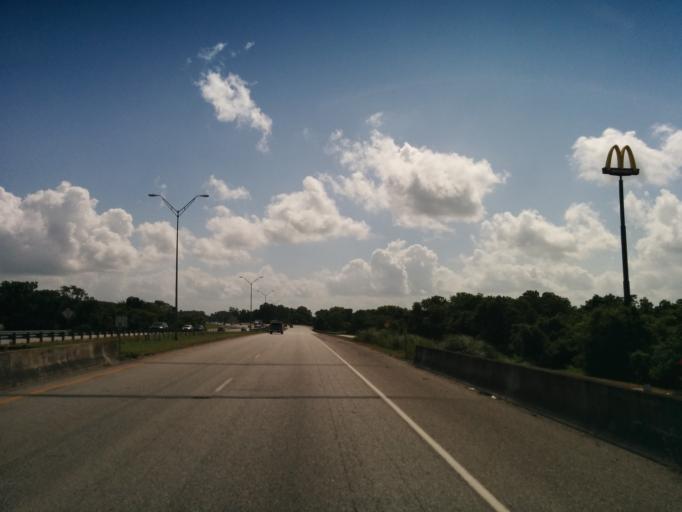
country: US
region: Texas
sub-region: Colorado County
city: Columbus
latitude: 29.6924
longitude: -96.5398
